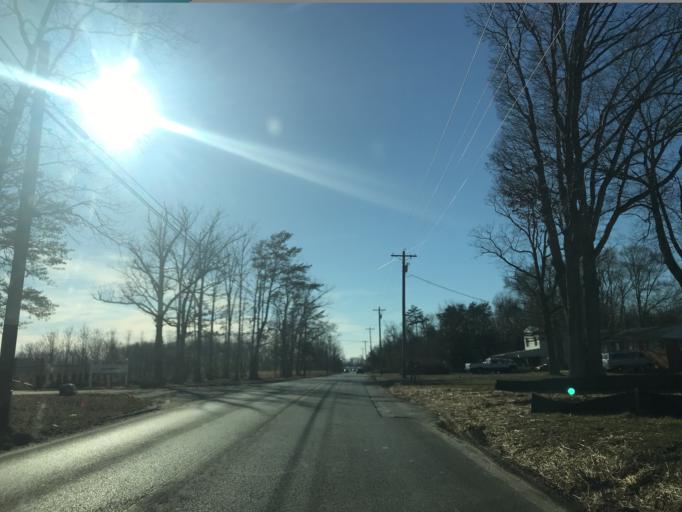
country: US
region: Maryland
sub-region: Charles County
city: Waldorf
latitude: 38.6740
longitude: -76.9477
